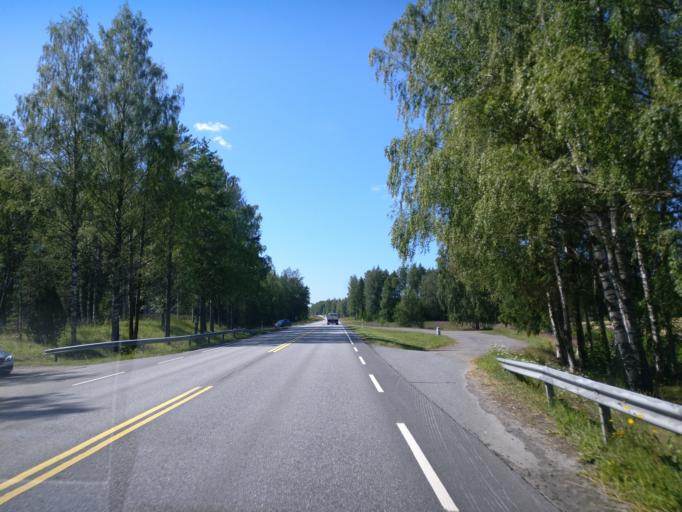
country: FI
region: Satakunta
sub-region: Pori
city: Kullaa
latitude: 61.4611
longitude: 22.1268
